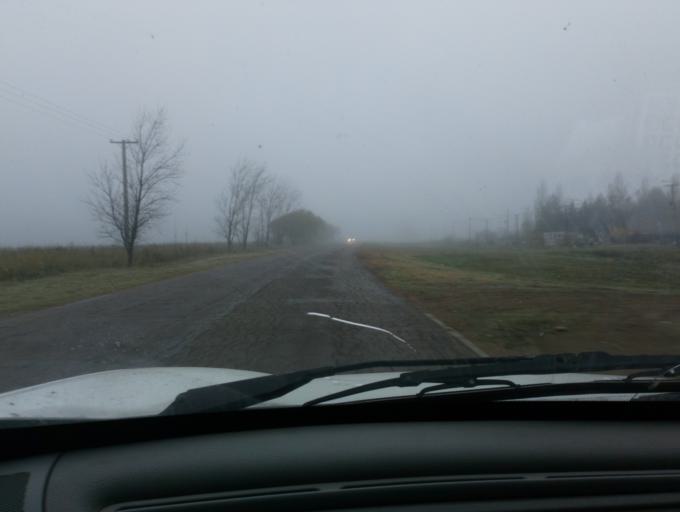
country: AR
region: La Pampa
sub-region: Departamento de Guatrache
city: Guatrache
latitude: -37.6648
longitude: -63.5187
